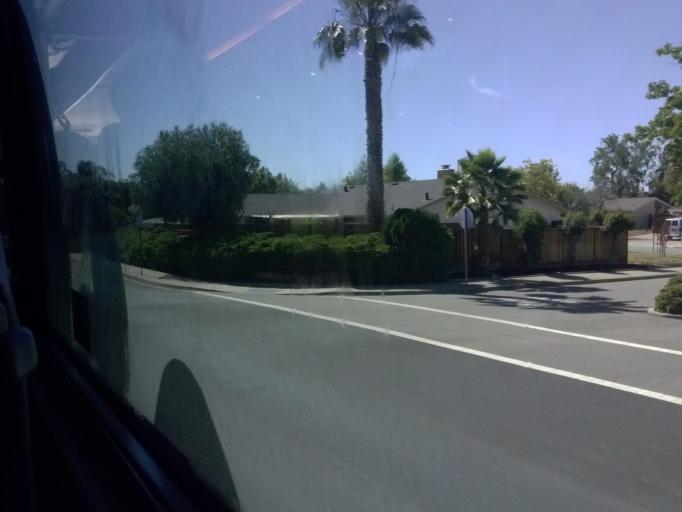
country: US
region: California
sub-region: Alameda County
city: Livermore
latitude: 37.6610
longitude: -121.7750
